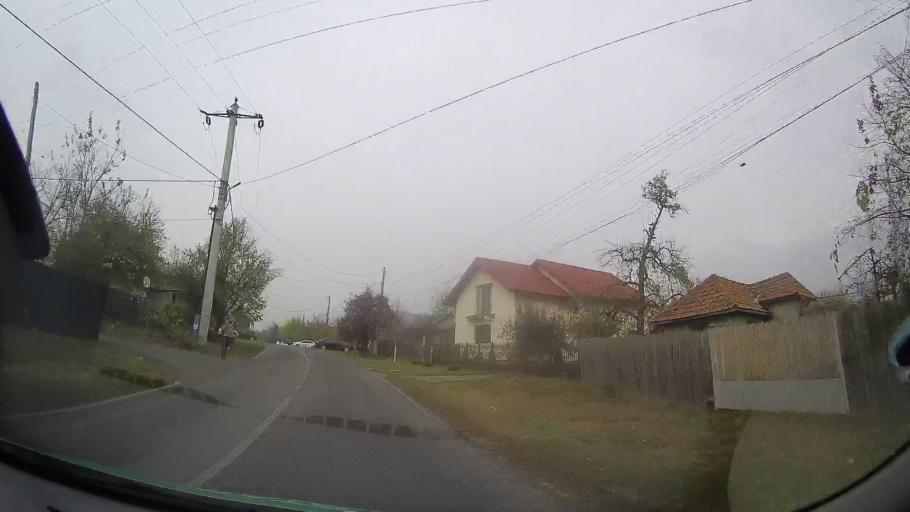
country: RO
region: Ilfov
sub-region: Comuna Gruiu
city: Gruiu
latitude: 44.7274
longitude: 26.2141
